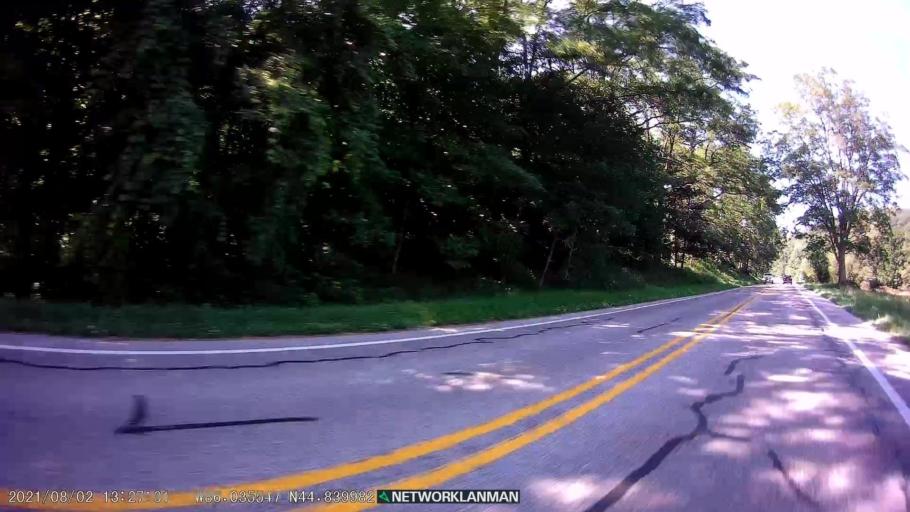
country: US
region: Michigan
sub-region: Benzie County
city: Beulah
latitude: 44.8403
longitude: -86.0355
